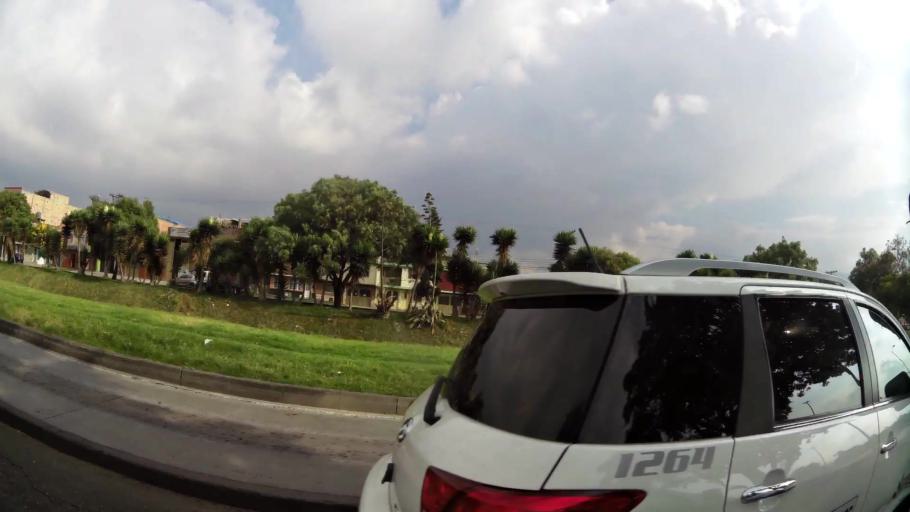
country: CO
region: Bogota D.C.
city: Bogota
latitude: 4.5692
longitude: -74.1337
